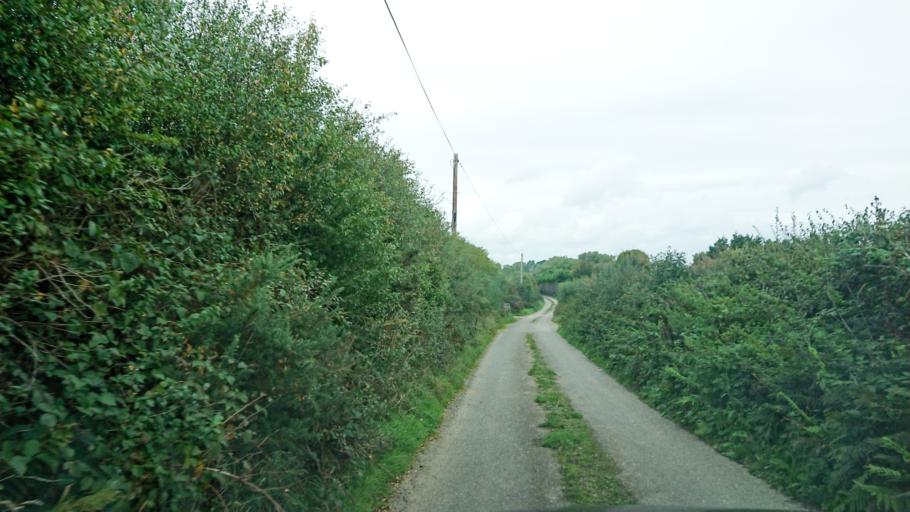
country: IE
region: Munster
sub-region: Waterford
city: Dunmore East
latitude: 52.2076
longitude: -7.0435
